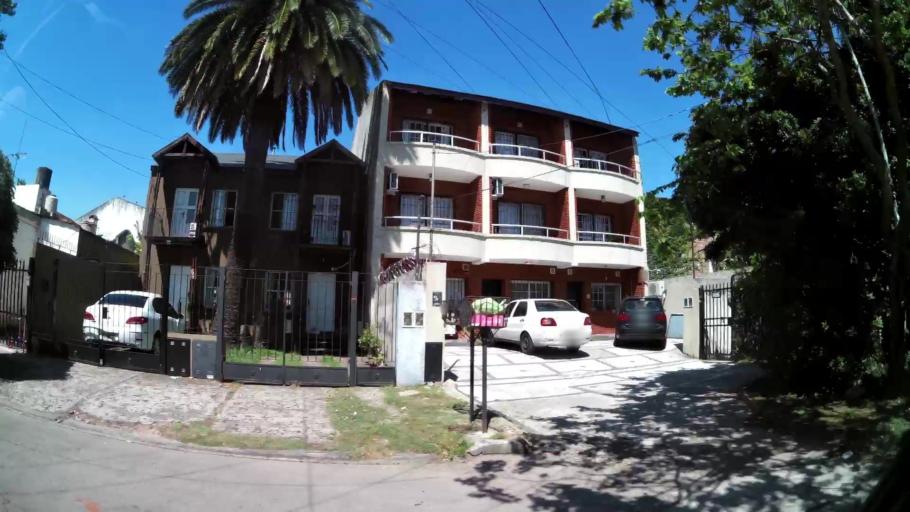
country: AR
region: Buenos Aires
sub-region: Partido de Tigre
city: Tigre
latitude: -34.4290
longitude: -58.5704
